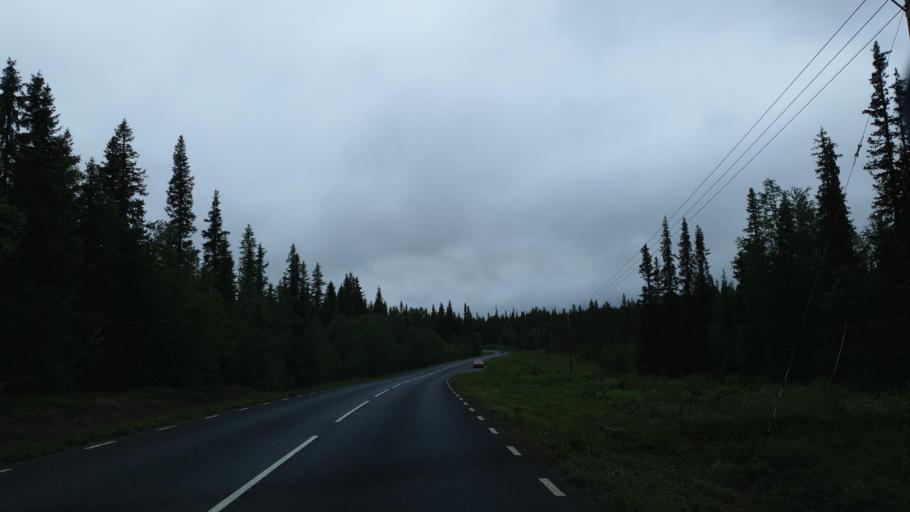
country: SE
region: Vaesterbotten
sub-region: Vilhelmina Kommun
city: Sjoberg
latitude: 65.2383
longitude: 15.7881
